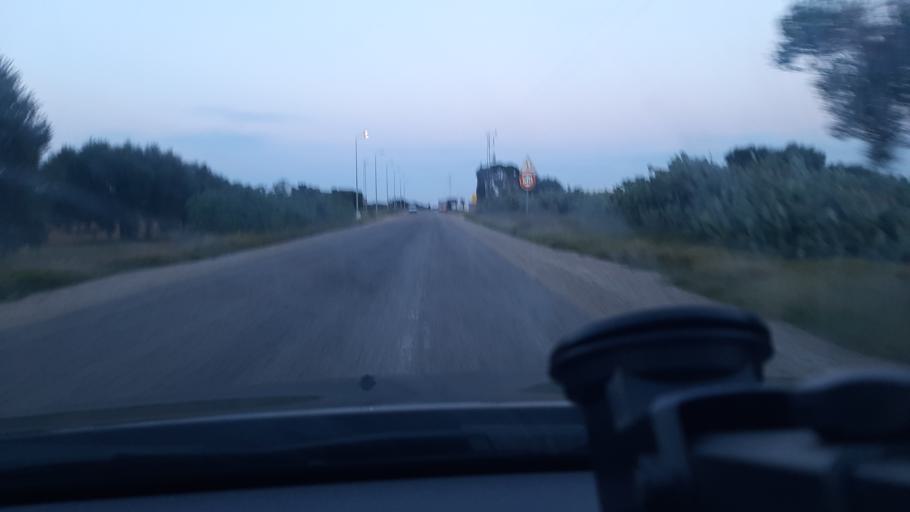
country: TN
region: Al Mahdiyah
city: Shurban
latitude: 35.0223
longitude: 10.4692
